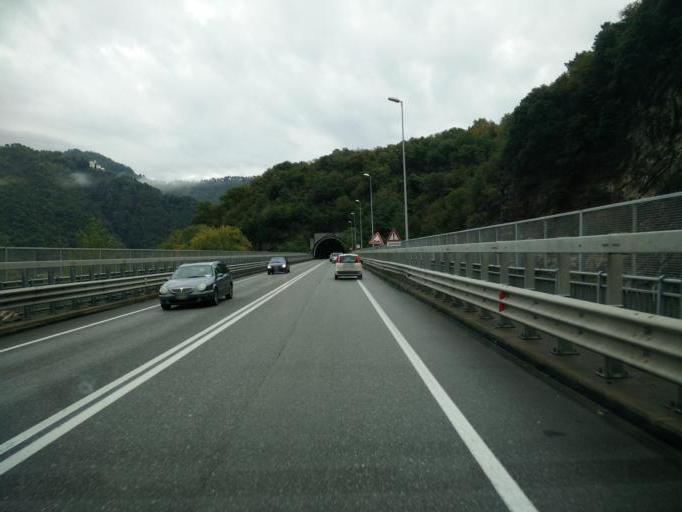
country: IT
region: Tuscany
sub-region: Provincia di Lucca
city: Valdottavo
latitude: 43.9257
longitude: 10.5198
